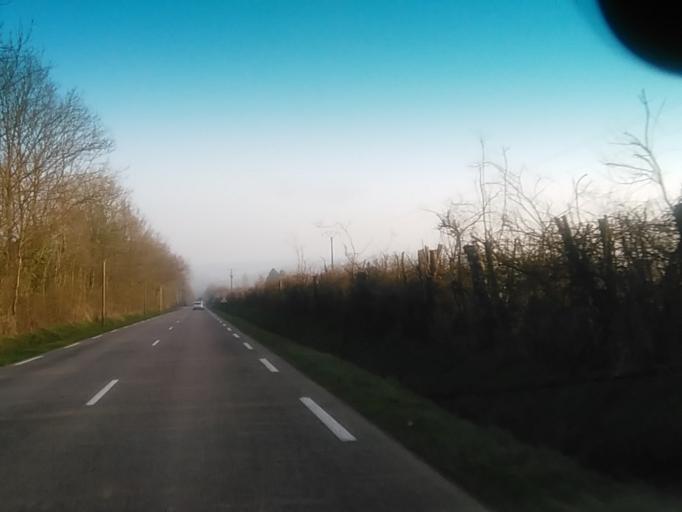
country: FR
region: Lower Normandy
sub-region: Departement du Calvados
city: Falaise
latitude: 48.8393
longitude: -0.2345
